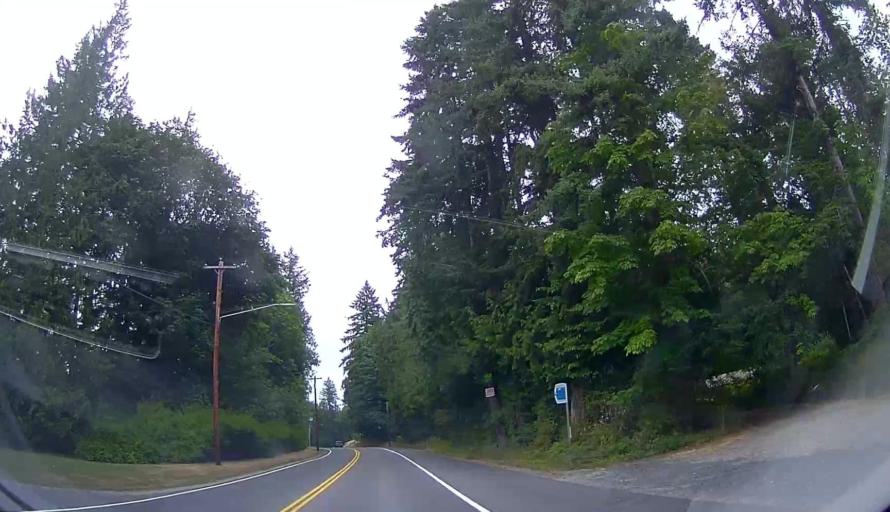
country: US
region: Washington
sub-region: Snohomish County
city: Warm Beach
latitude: 48.1844
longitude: -122.3468
